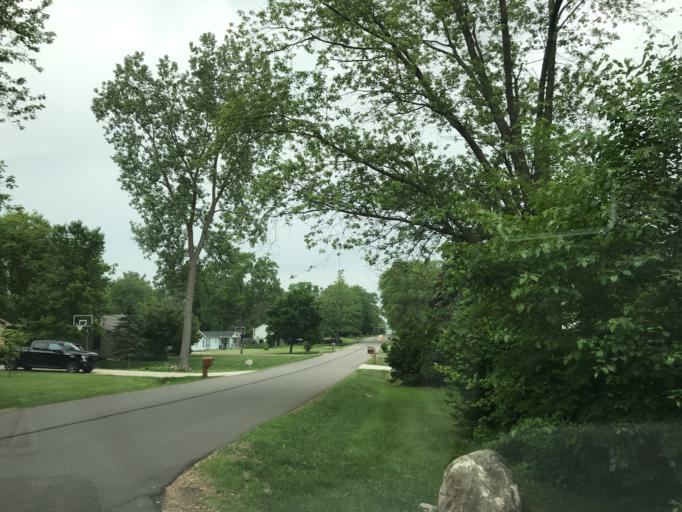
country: US
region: Michigan
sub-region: Oakland County
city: Novi
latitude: 42.4766
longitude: -83.4840
